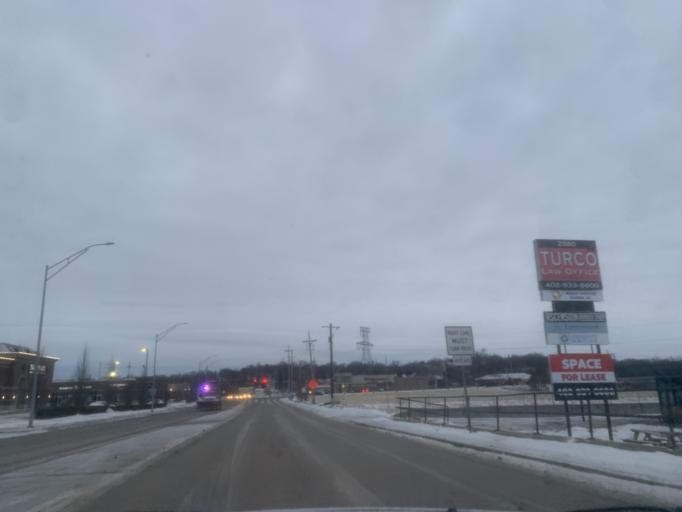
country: US
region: Nebraska
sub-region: Douglas County
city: Ralston
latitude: 41.2361
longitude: -96.0526
